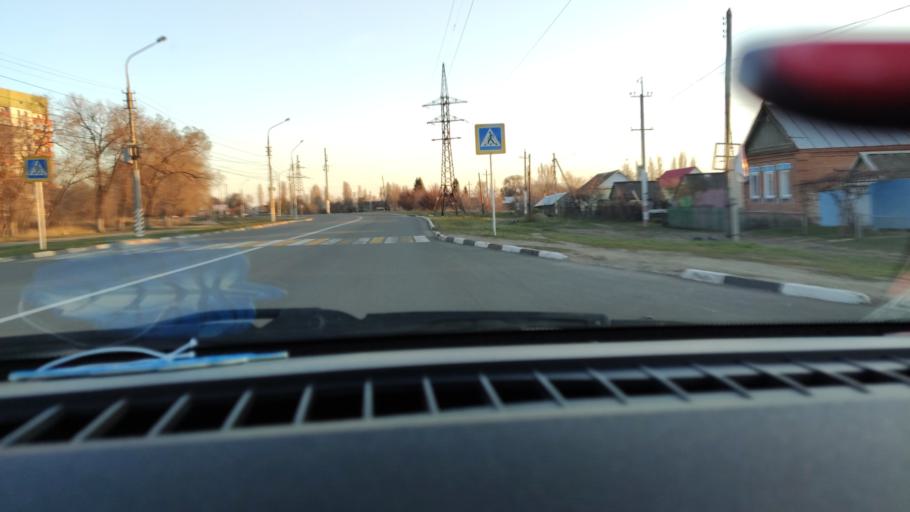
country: RU
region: Saratov
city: Privolzhskiy
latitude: 51.3941
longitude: 46.0342
